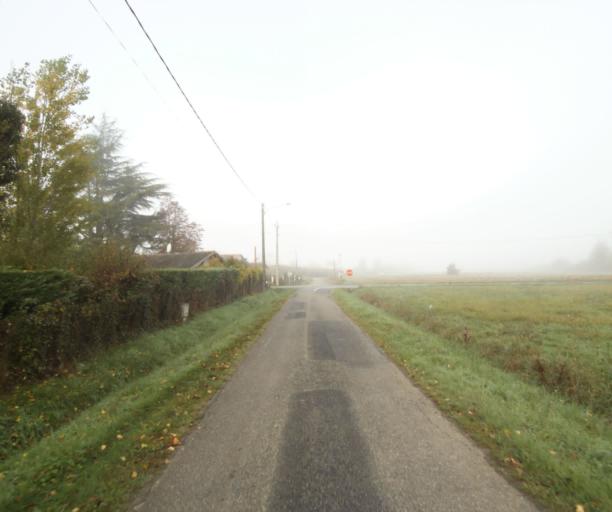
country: FR
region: Midi-Pyrenees
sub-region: Departement du Tarn-et-Garonne
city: Nohic
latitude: 43.8961
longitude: 1.4455
